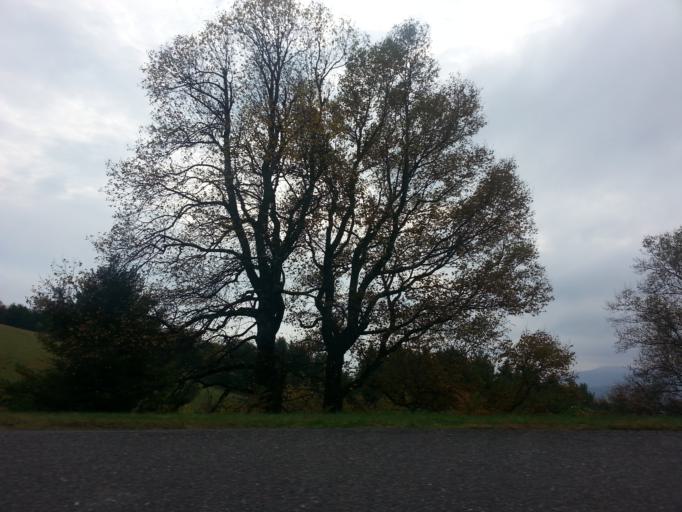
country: US
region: North Carolina
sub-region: Wilkes County
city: Millers Creek
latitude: 36.2766
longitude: -81.3798
